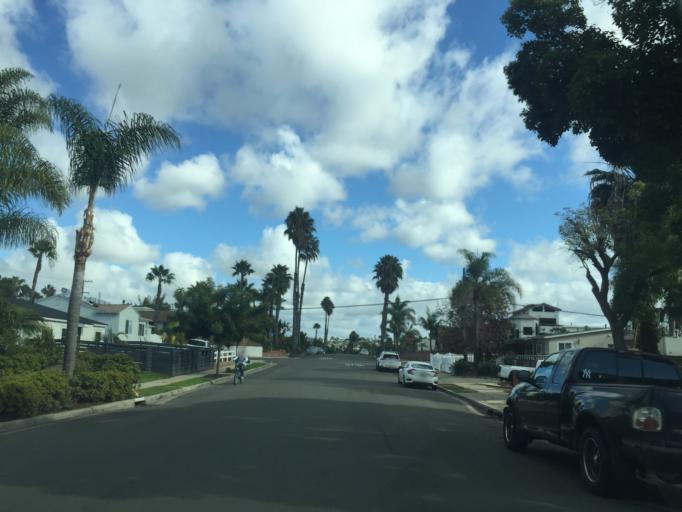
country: US
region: California
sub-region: San Diego County
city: La Jolla
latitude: 32.7987
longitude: -117.2316
